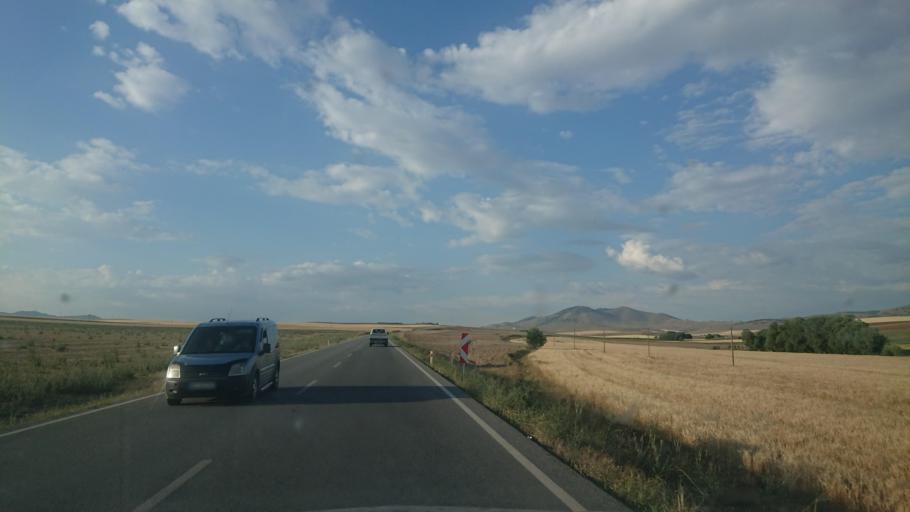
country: TR
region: Aksaray
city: Aksaray
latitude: 38.4870
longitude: 34.0680
